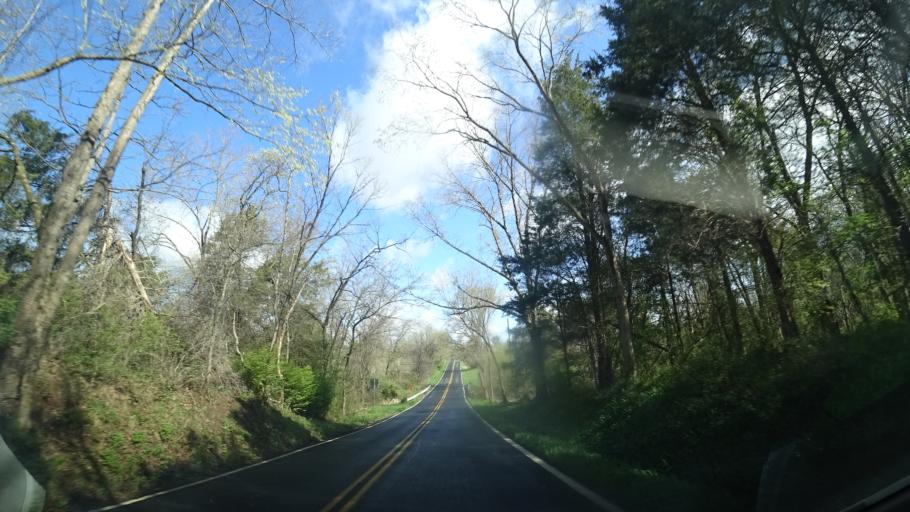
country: US
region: Maryland
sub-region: Montgomery County
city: Poolesville
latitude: 39.1134
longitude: -77.3805
